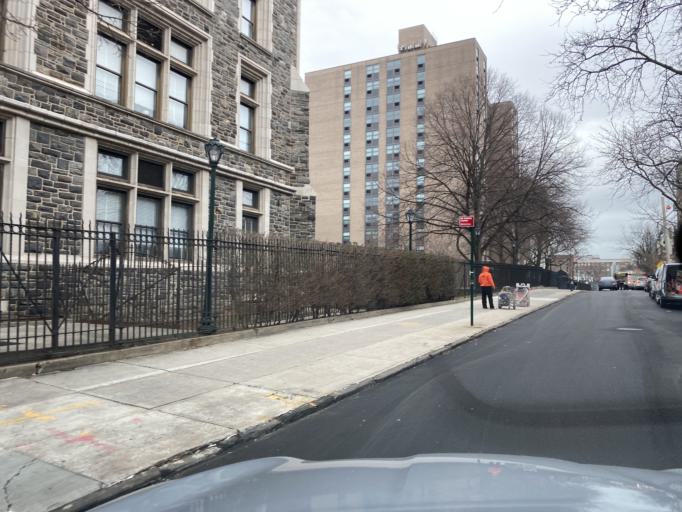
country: US
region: New York
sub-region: Bronx
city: The Bronx
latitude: 40.8601
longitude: -73.8867
